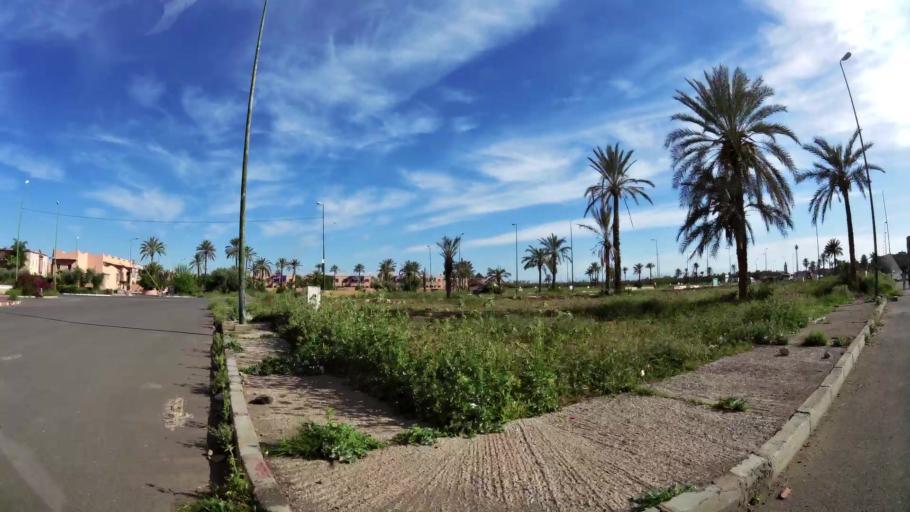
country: MA
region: Marrakech-Tensift-Al Haouz
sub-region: Marrakech
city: Marrakesh
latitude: 31.6783
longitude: -8.0564
